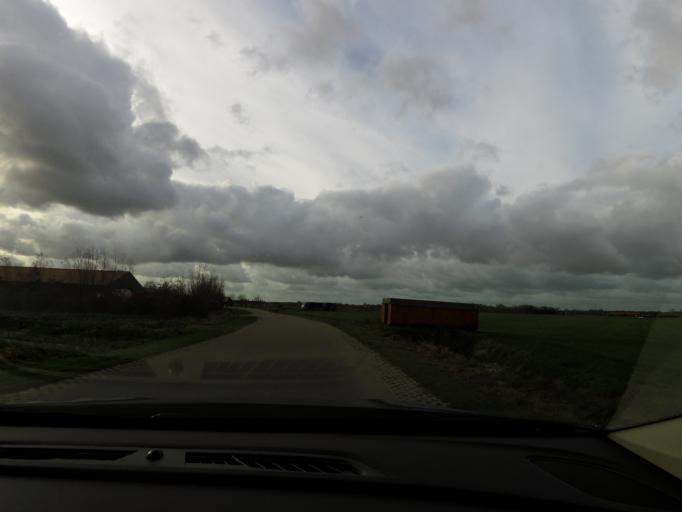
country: NL
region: Zeeland
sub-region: Schouwen-Duiveland
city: Renesse
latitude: 51.7274
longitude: 3.8000
